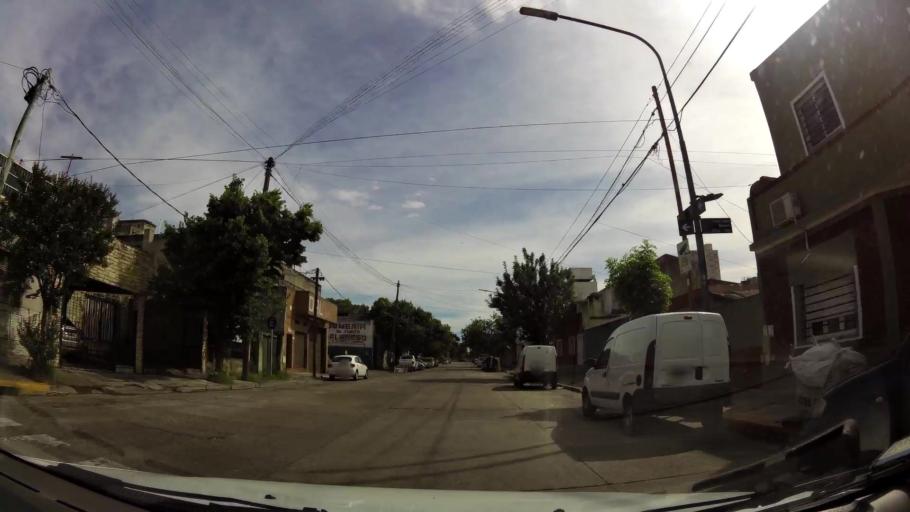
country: AR
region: Buenos Aires F.D.
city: Villa Lugano
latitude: -34.6655
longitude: -58.5096
